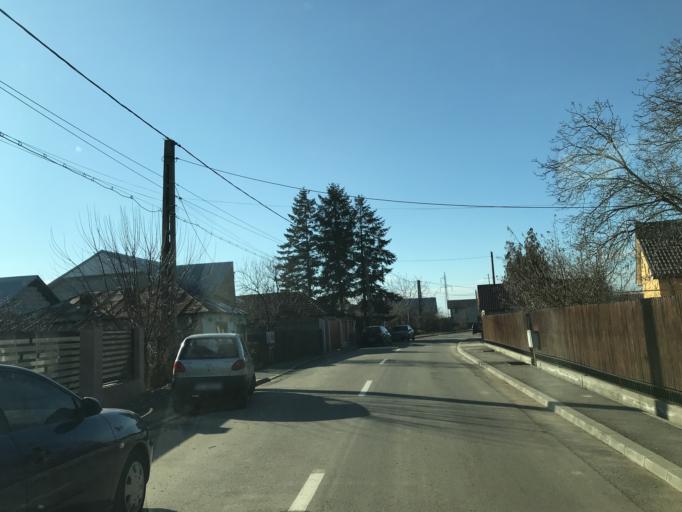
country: RO
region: Olt
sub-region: Municipiul Slatina
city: Slatina
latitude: 44.4517
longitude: 24.3679
